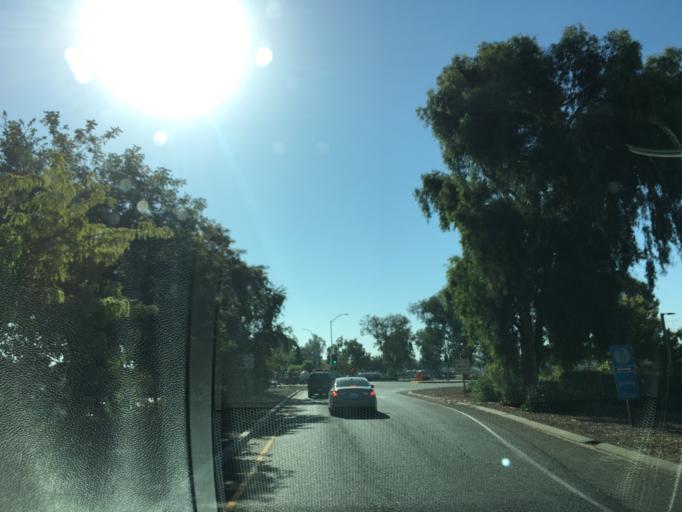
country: US
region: California
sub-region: Madera County
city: Madera
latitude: 36.9754
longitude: -120.0777
